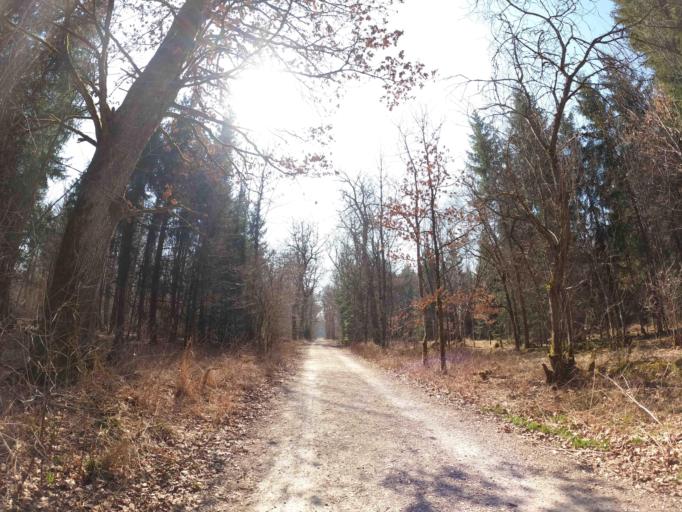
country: DE
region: Bavaria
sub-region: Upper Bavaria
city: Neuried
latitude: 48.0528
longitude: 11.4527
